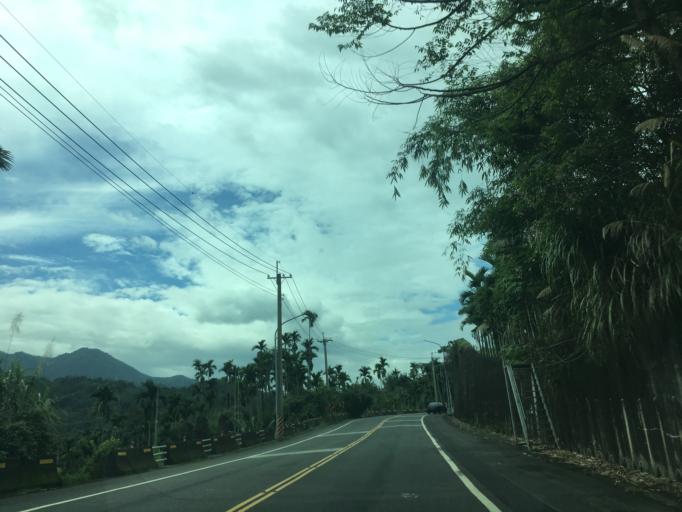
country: TW
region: Taiwan
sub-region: Yunlin
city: Douliu
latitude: 23.5758
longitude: 120.5642
